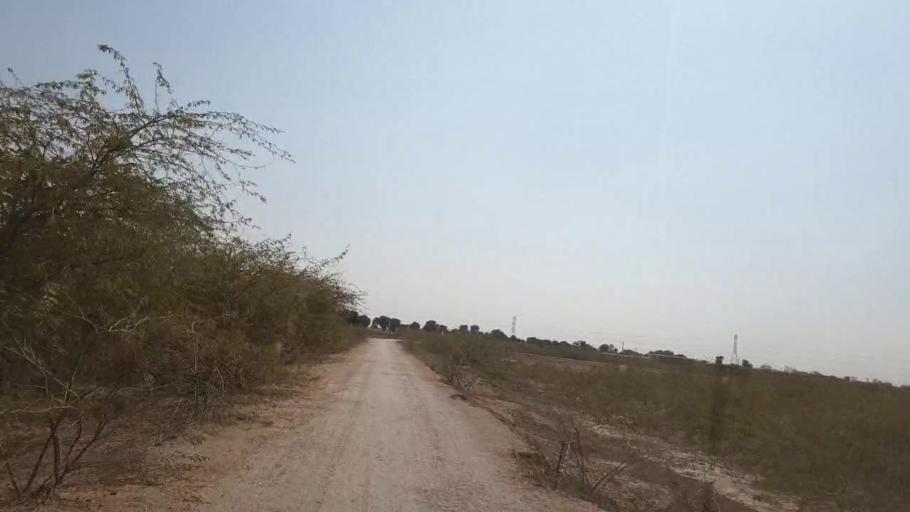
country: PK
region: Sindh
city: Nabisar
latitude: 25.0665
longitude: 69.5478
